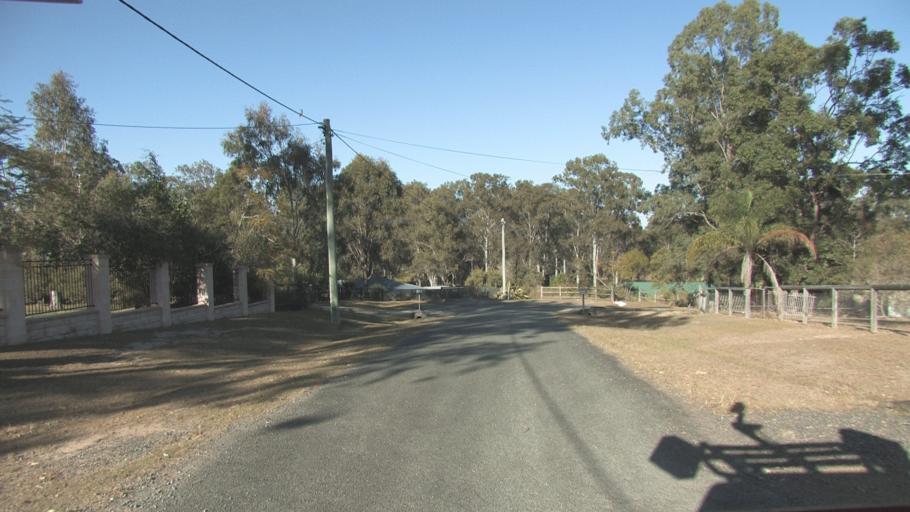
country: AU
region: Queensland
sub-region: Logan
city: Cedar Vale
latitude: -27.8415
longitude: 153.0107
